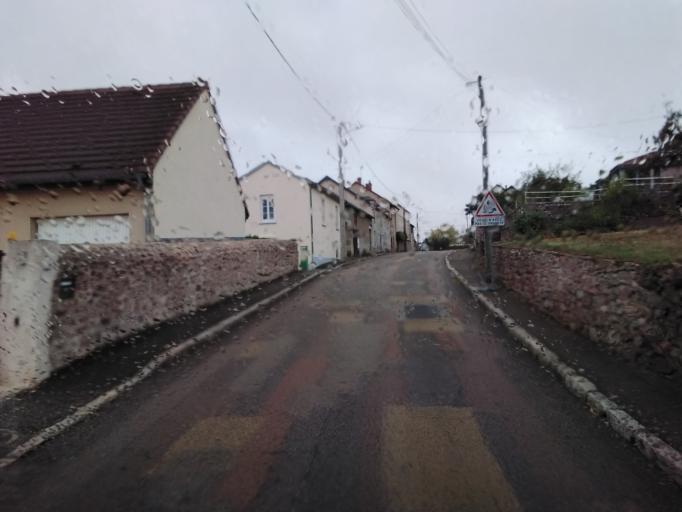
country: FR
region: Bourgogne
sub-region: Departement de la Cote-d'Or
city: Saulieu
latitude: 47.2764
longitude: 4.2261
